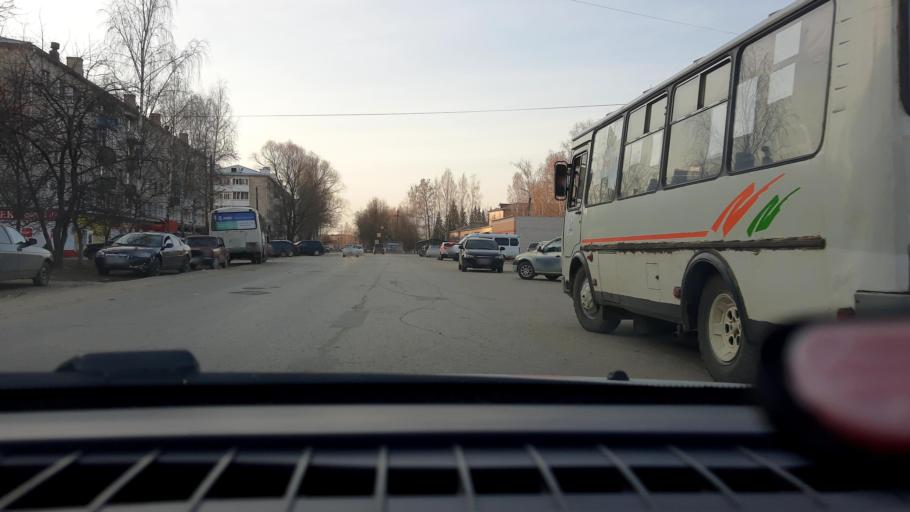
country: RU
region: Nizjnij Novgorod
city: Bogorodsk
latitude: 56.1002
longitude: 43.4794
